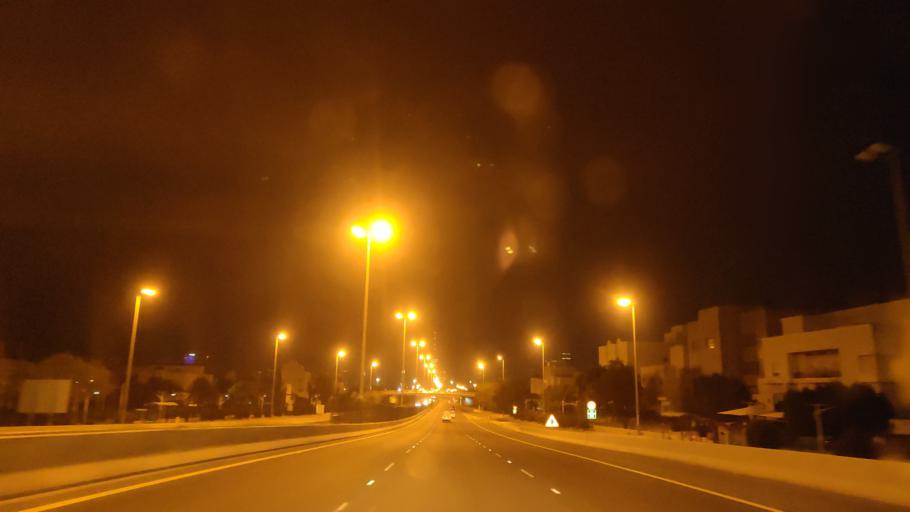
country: KW
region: Al Asimah
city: Ash Shamiyah
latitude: 29.3337
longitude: 47.9714
